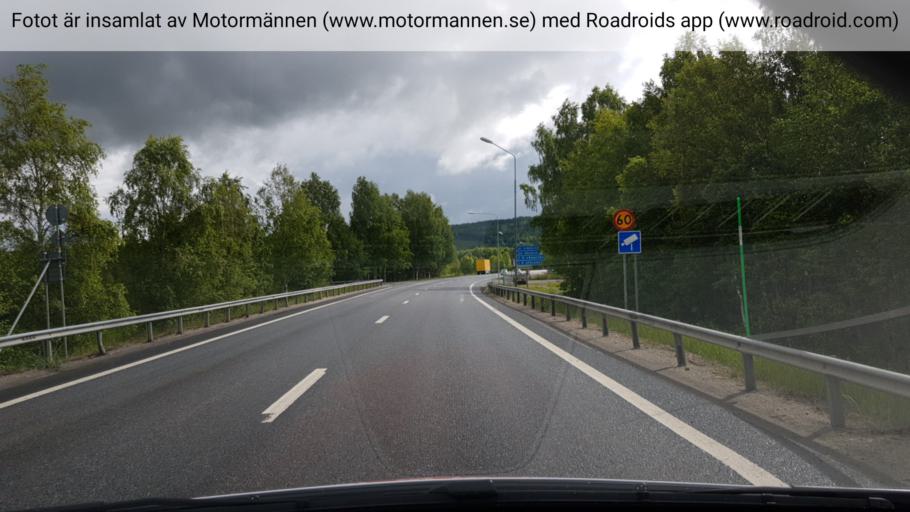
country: SE
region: Vaesterbotten
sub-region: Vannas Kommun
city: Vannasby
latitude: 63.9215
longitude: 19.8564
